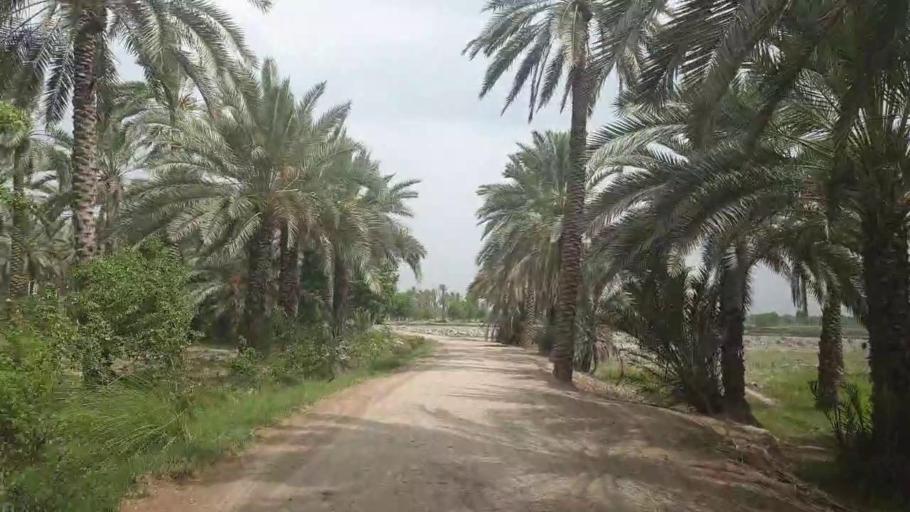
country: PK
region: Sindh
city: Khairpur
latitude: 27.5807
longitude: 68.7409
